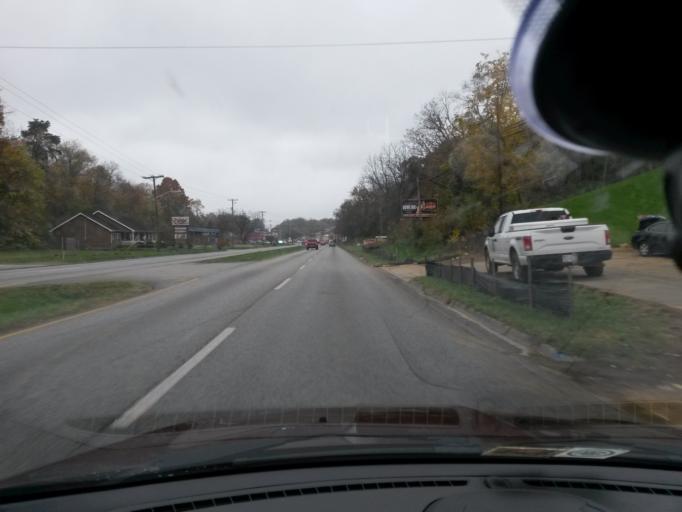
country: US
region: Virginia
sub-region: Roanoke County
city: Vinton
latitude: 37.2928
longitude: -79.9061
